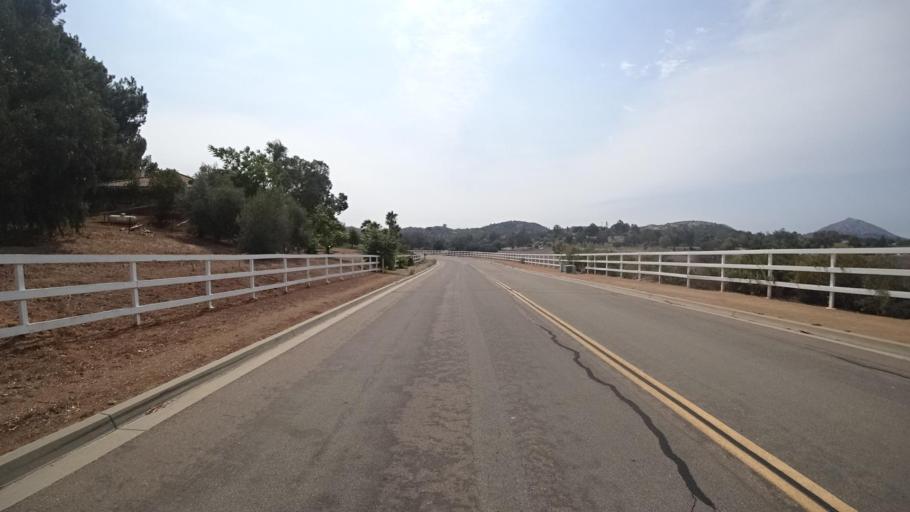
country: US
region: California
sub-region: San Diego County
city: Ramona
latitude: 33.0067
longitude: -116.8945
